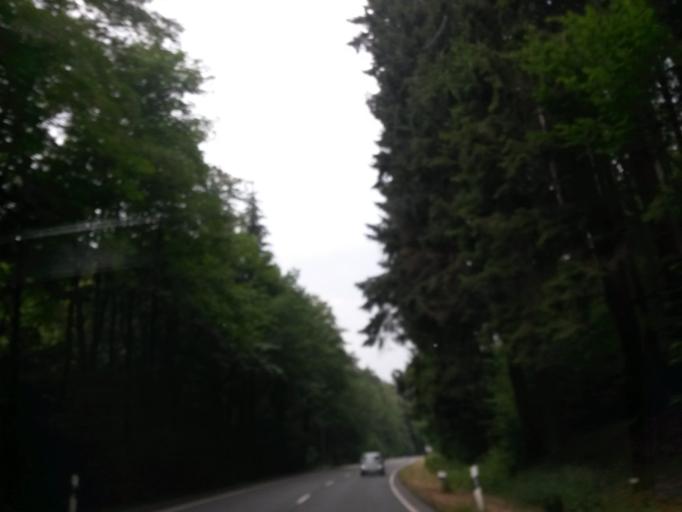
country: DE
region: North Rhine-Westphalia
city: Meinerzhagen
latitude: 51.0752
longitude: 7.6482
